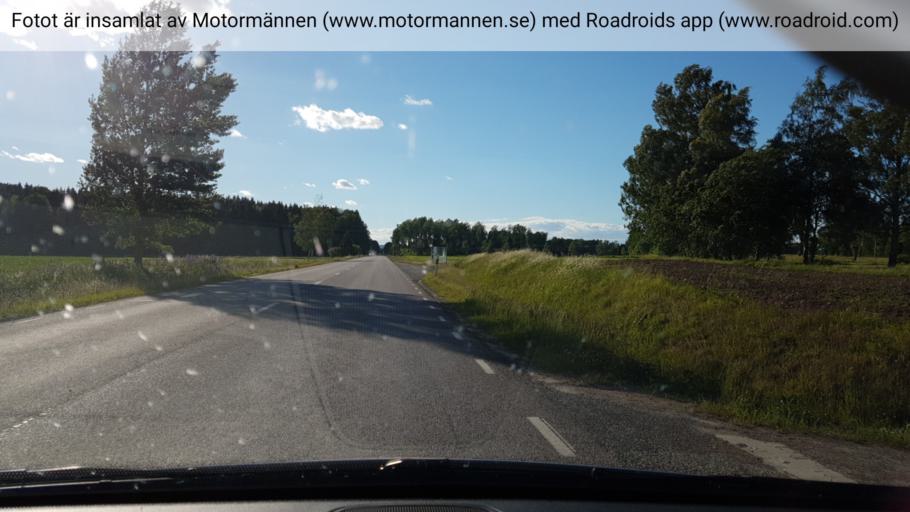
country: SE
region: Vaestra Goetaland
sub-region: Tidaholms Kommun
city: Olofstorp
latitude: 58.3624
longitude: 14.0285
